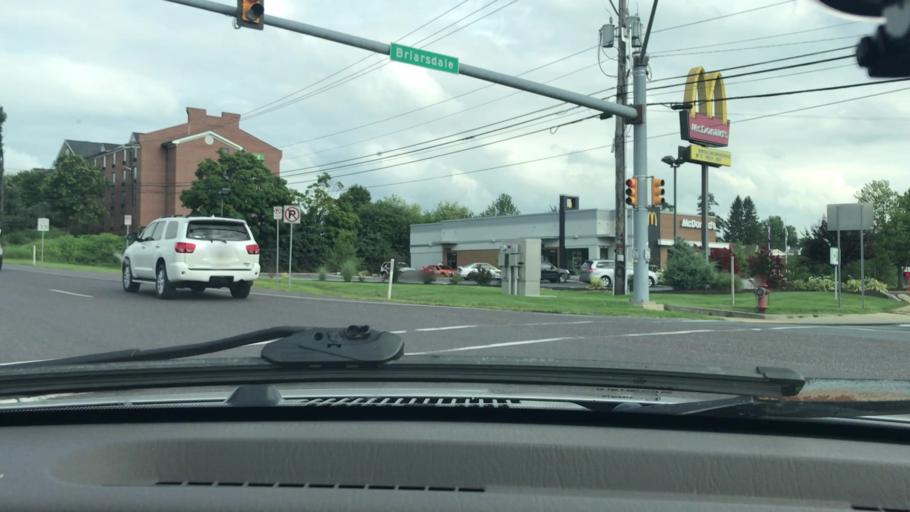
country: US
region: Pennsylvania
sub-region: Dauphin County
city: Progress
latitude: 40.2783
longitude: -76.8225
